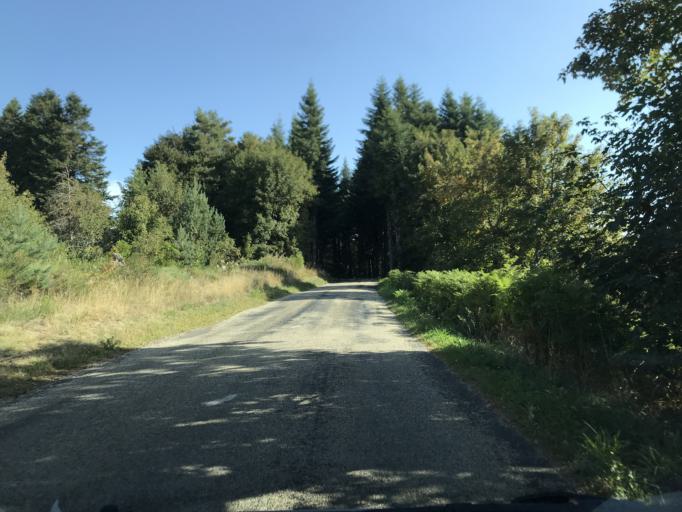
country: FR
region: Rhone-Alpes
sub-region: Departement de l'Ardeche
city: Saint-Agreve
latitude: 45.0298
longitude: 4.4225
